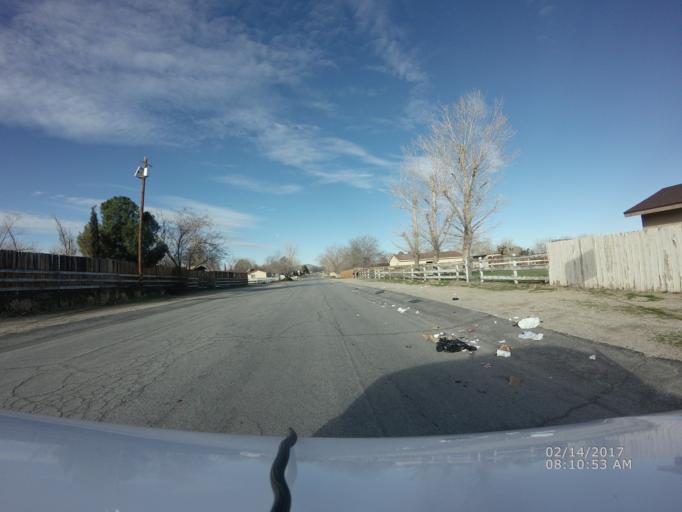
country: US
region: California
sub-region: Los Angeles County
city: Littlerock
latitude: 34.5538
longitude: -117.9585
